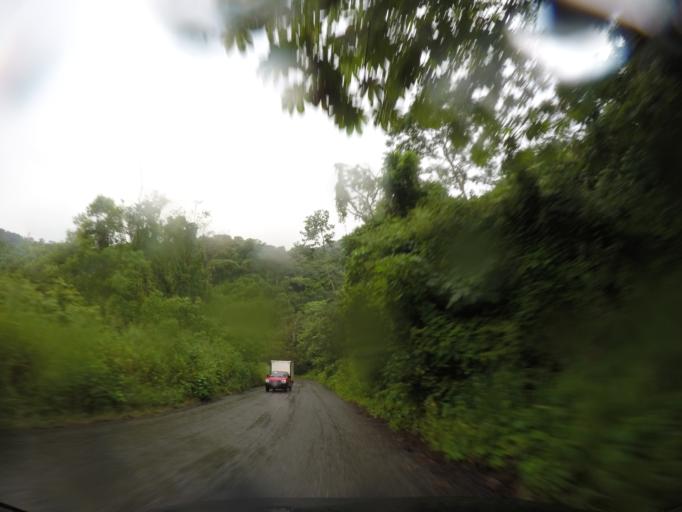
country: MX
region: Oaxaca
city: San Gabriel Mixtepec
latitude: 16.0574
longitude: -97.0802
